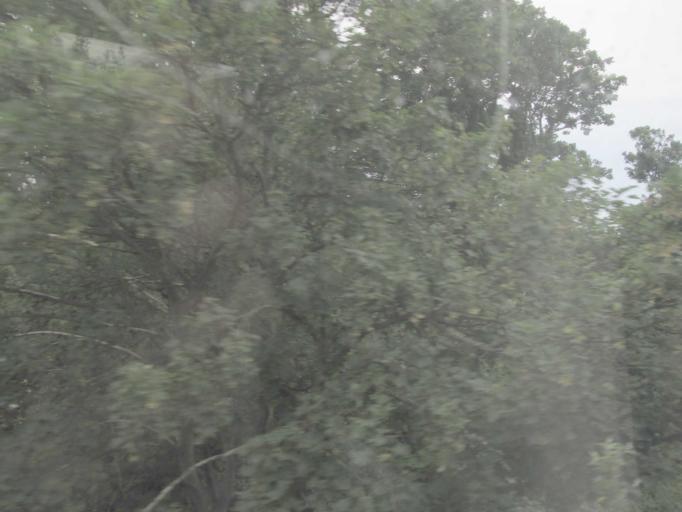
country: GB
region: England
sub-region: Greater London
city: Greenford
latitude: 51.5111
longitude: -0.3438
